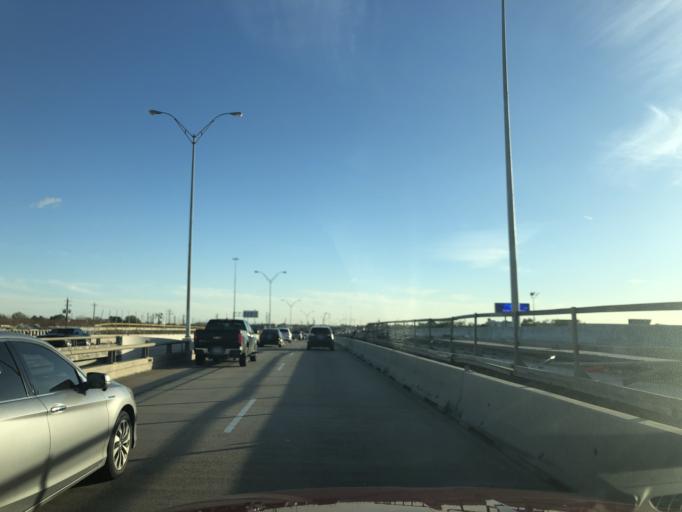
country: US
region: Texas
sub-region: Harris County
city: Deer Park
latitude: 29.6657
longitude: -95.1559
